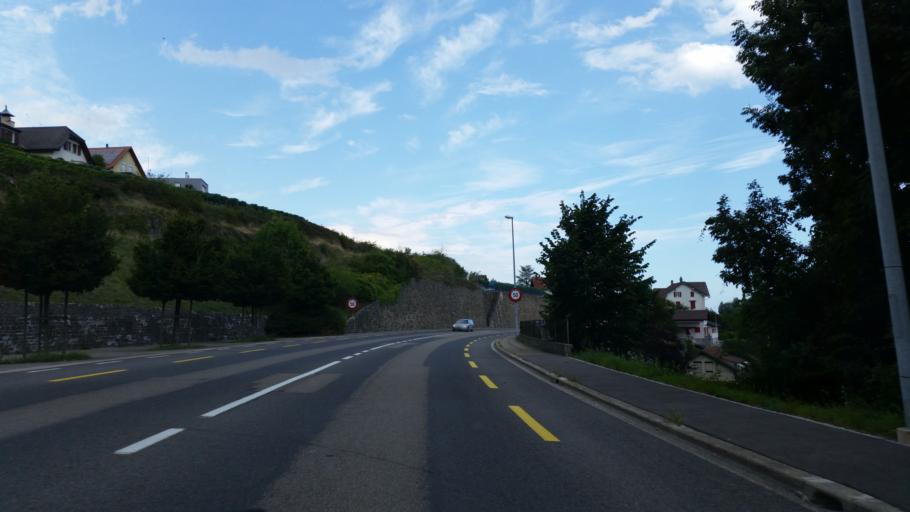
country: CH
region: Neuchatel
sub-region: Boudry District
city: Saint-Aubin-Sauges
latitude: 46.8907
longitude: 6.7690
